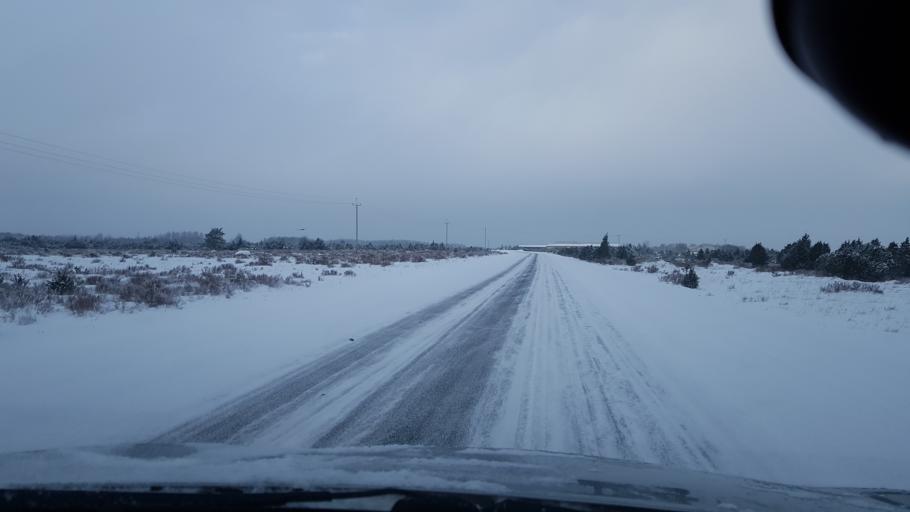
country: EE
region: Harju
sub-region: Keila linn
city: Keila
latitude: 59.3810
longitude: 24.4027
